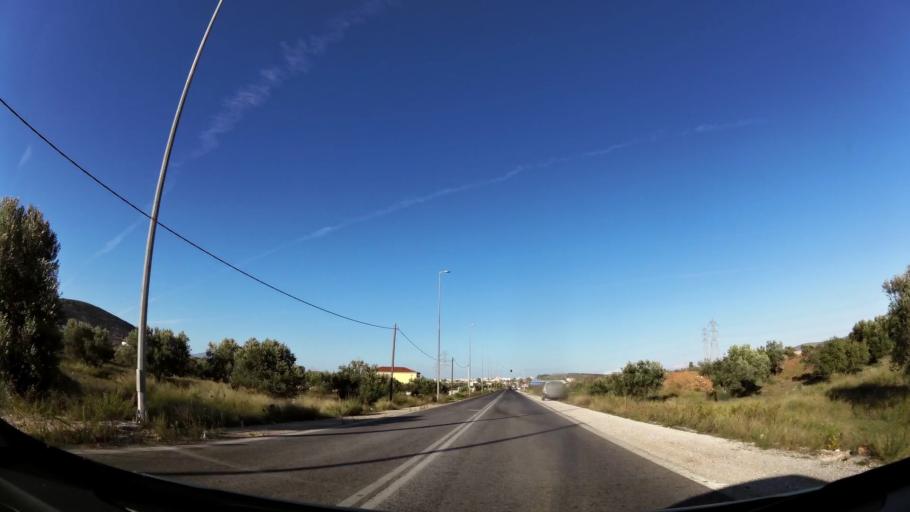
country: GR
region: Attica
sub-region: Nomarchia Anatolikis Attikis
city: Kalyvia Thorikou
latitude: 37.8610
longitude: 23.9228
